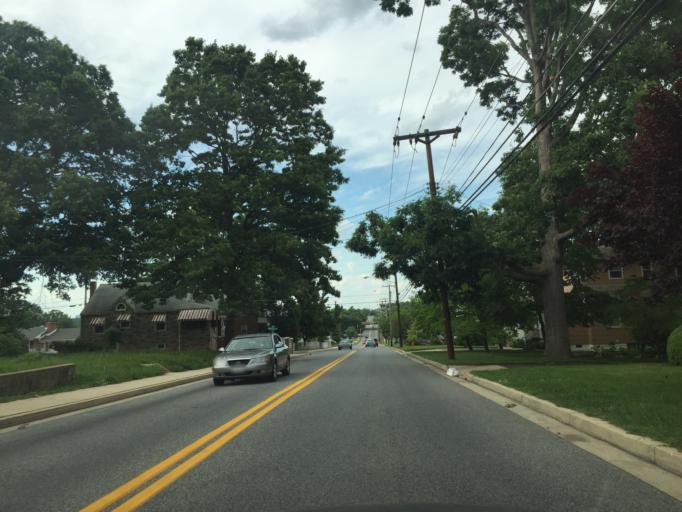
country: US
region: Maryland
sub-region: Baltimore County
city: Essex
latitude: 39.3176
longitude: -76.4749
